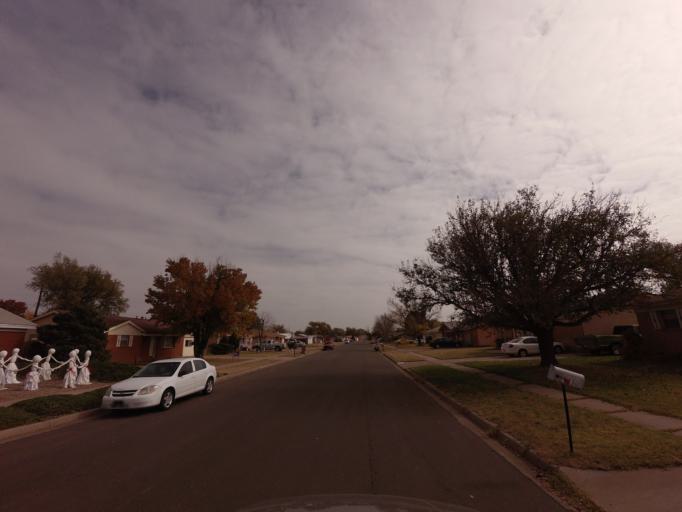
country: US
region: New Mexico
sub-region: Curry County
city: Clovis
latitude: 34.4306
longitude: -103.2216
